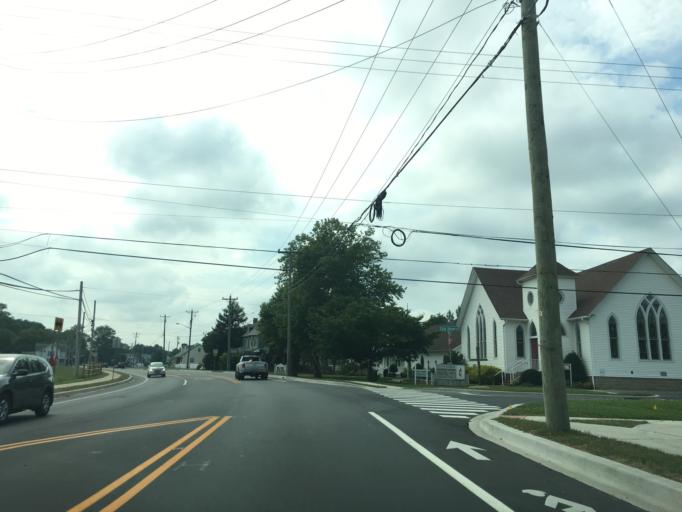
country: US
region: Delaware
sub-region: Sussex County
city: Ocean View
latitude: 38.5478
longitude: -75.1137
